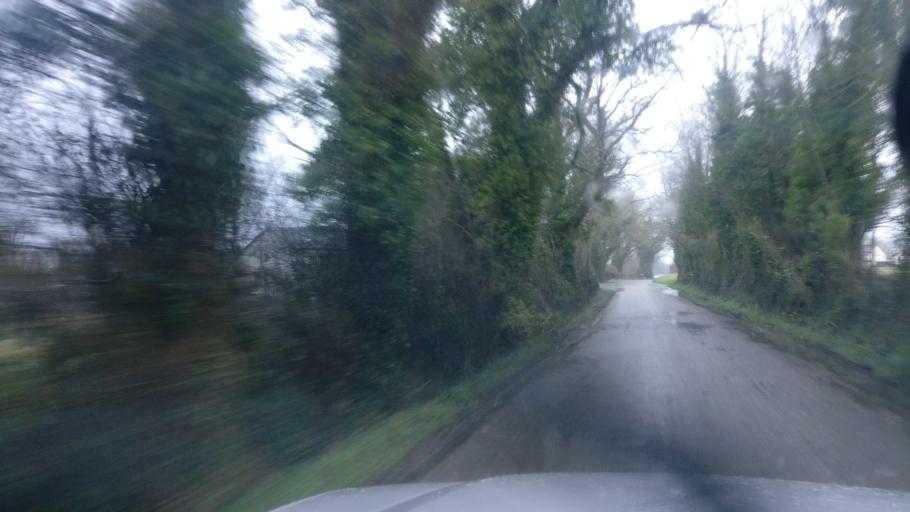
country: IE
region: Connaught
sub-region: County Galway
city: Ballinasloe
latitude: 53.3076
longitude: -8.3413
